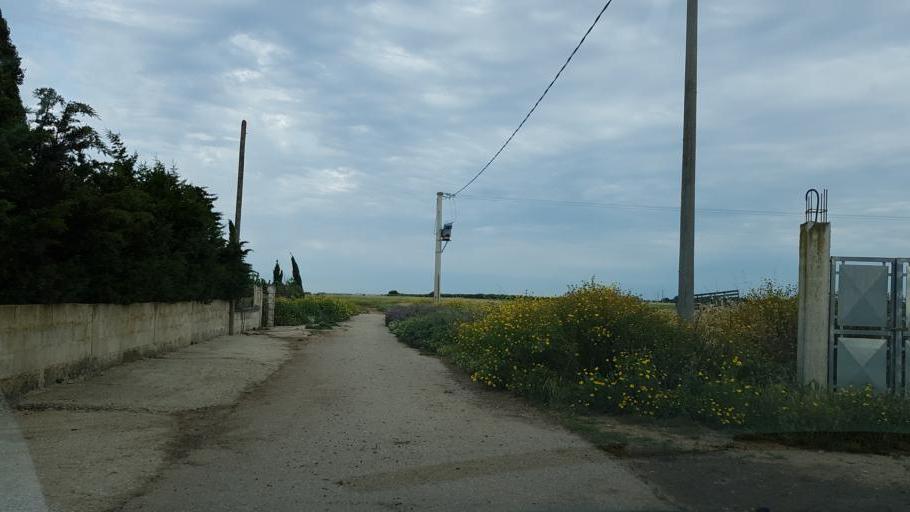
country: IT
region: Apulia
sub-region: Provincia di Brindisi
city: Brindisi
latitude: 40.6548
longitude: 17.8690
